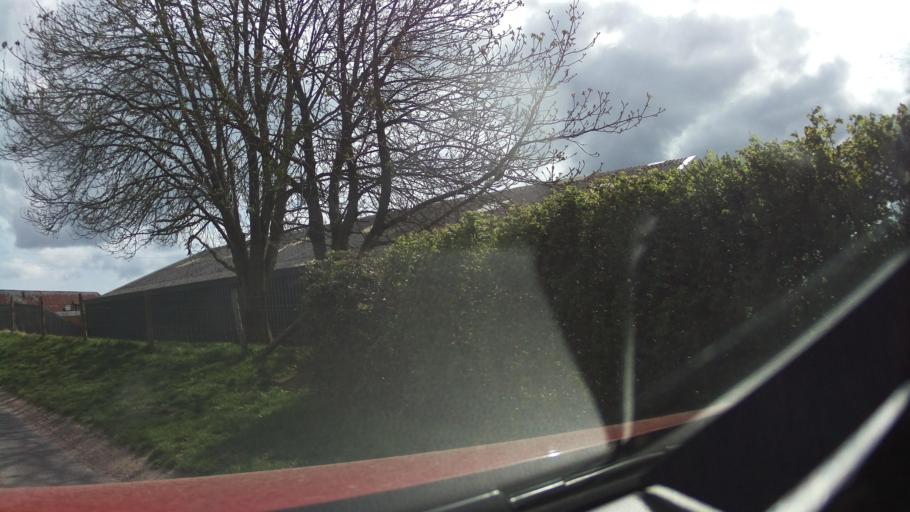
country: GB
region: England
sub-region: Hampshire
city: Romsey
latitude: 51.0289
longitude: -1.5007
